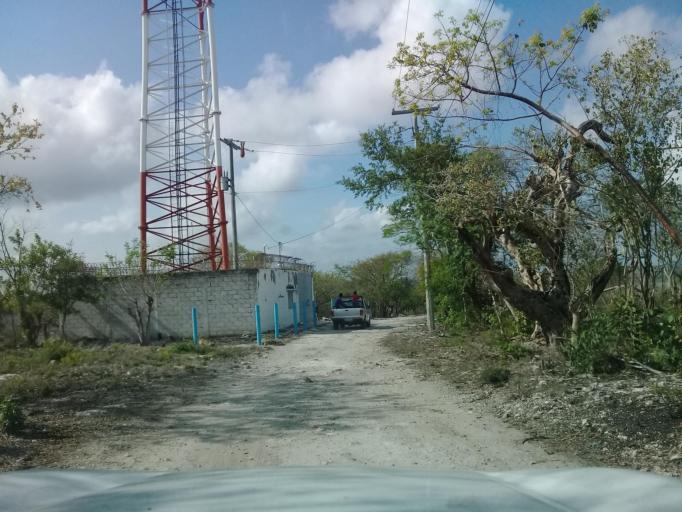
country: MX
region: Veracruz
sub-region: Emiliano Zapata
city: Plan del Rio
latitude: 19.4111
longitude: -96.6515
